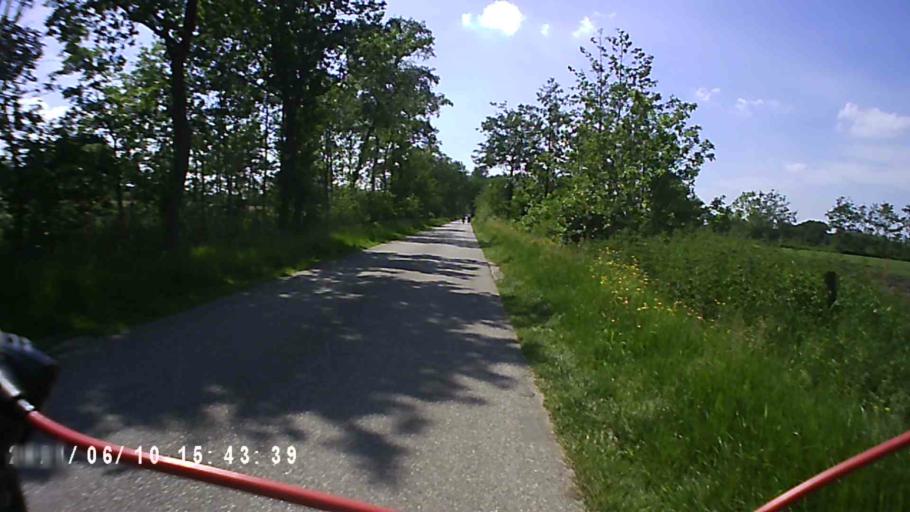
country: NL
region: Friesland
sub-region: Gemeente Achtkarspelen
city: Boelenslaan
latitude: 53.1664
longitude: 6.1380
